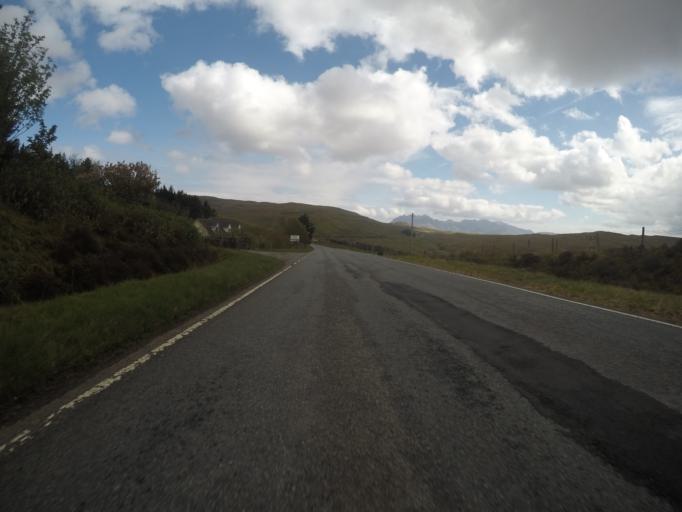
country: GB
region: Scotland
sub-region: Highland
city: Isle of Skye
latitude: 57.3316
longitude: -6.3435
